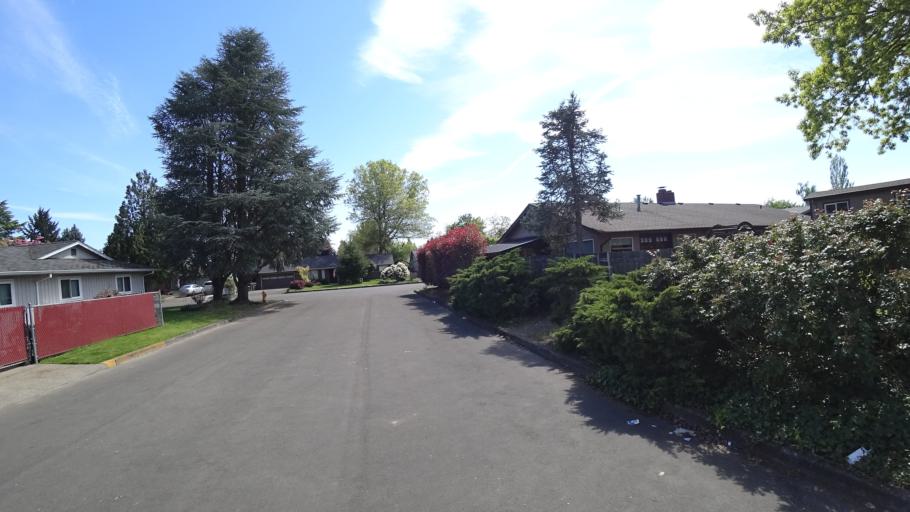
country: US
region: Oregon
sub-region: Washington County
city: Hillsboro
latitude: 45.5112
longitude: -122.9562
